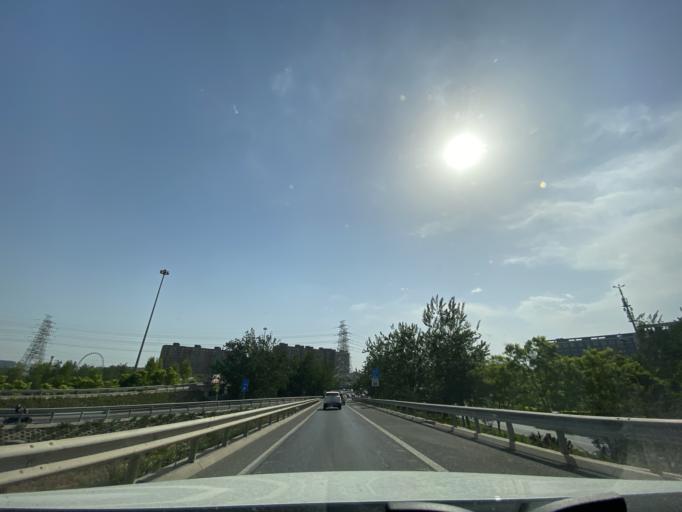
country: CN
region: Beijing
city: Lugu
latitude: 39.9246
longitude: 116.2046
